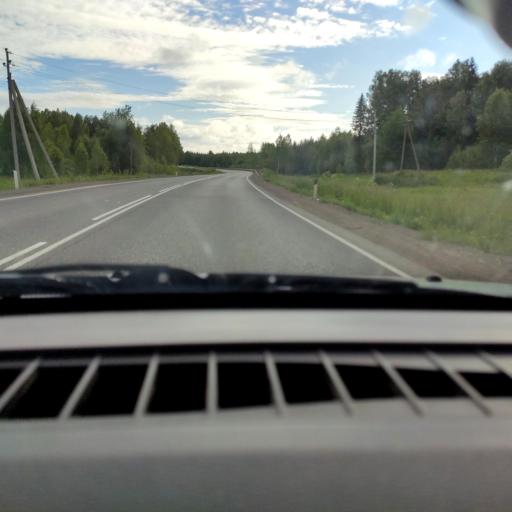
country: RU
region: Perm
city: Kungur
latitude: 57.3308
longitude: 56.9620
